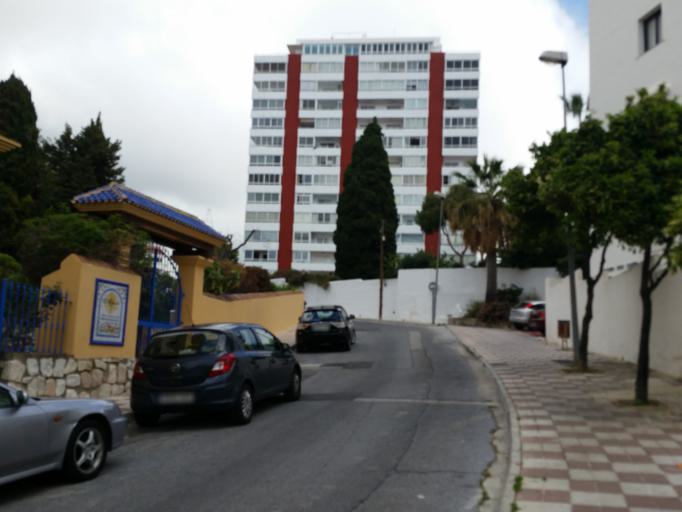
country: ES
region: Andalusia
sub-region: Provincia de Malaga
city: Torremolinos
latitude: 36.5935
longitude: -4.5244
